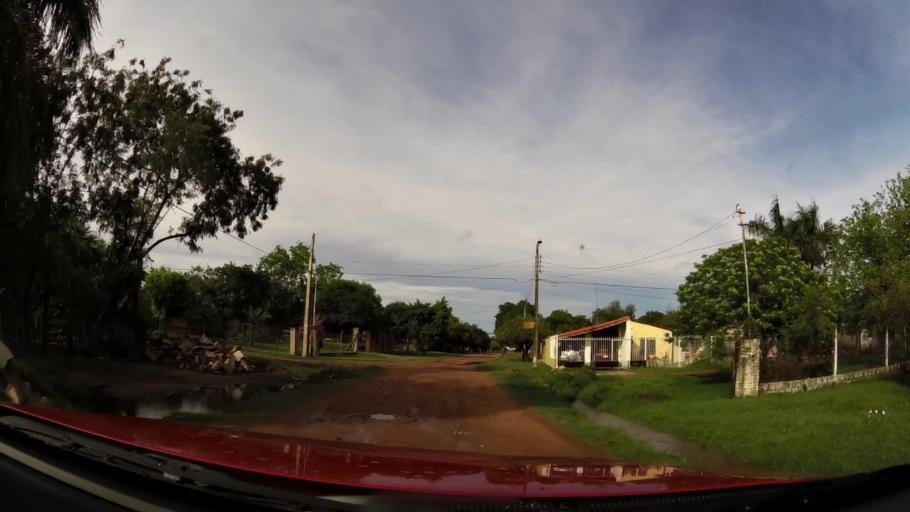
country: PY
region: Central
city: Limpio
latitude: -25.1864
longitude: -57.4813
